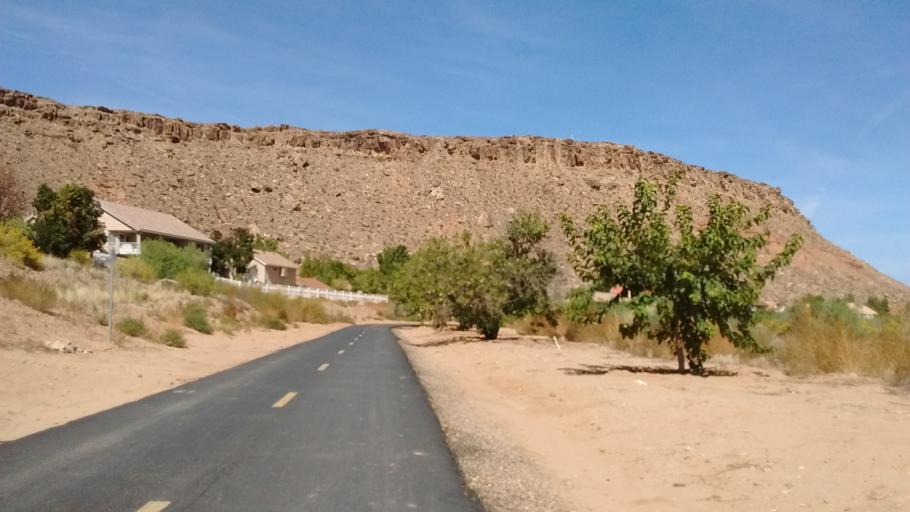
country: US
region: Utah
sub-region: Washington County
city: Saint George
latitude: 37.0601
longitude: -113.5981
